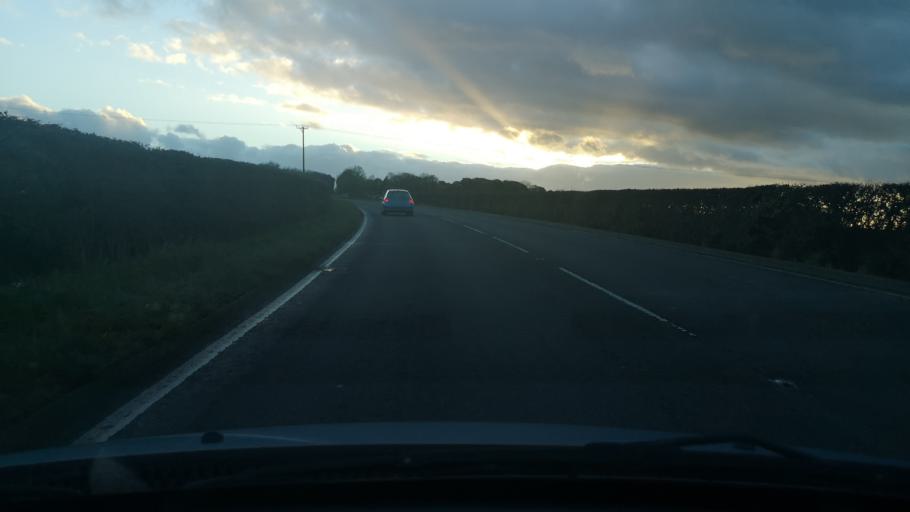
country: GB
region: England
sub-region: City and Borough of Wakefield
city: Middlestown
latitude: 53.6270
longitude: -1.5740
